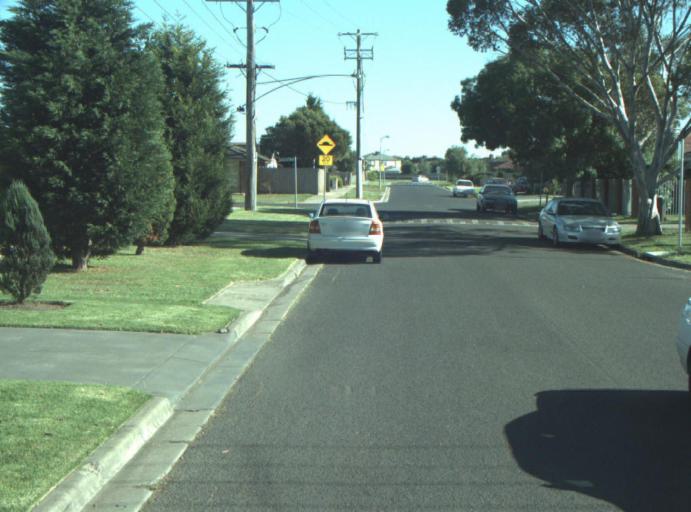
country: AU
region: Victoria
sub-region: Greater Geelong
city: Hamlyn Heights
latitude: -38.1128
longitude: 144.3228
